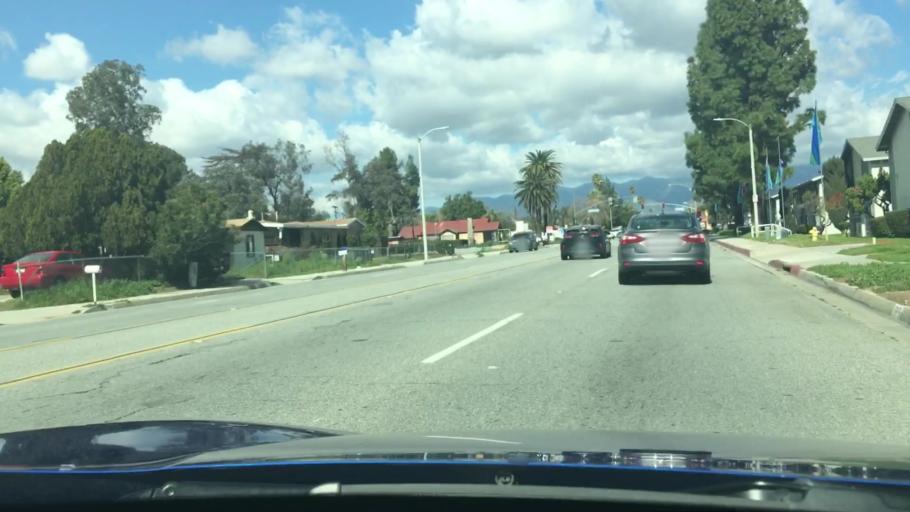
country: US
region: California
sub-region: San Bernardino County
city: Rialto
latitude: 34.0834
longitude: -117.3702
